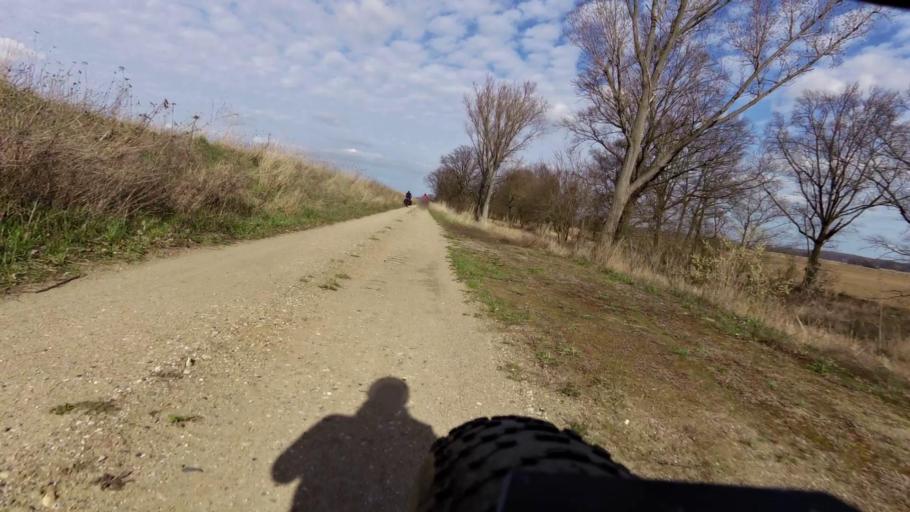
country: DE
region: Brandenburg
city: Reitwein
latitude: 52.4527
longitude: 14.5984
